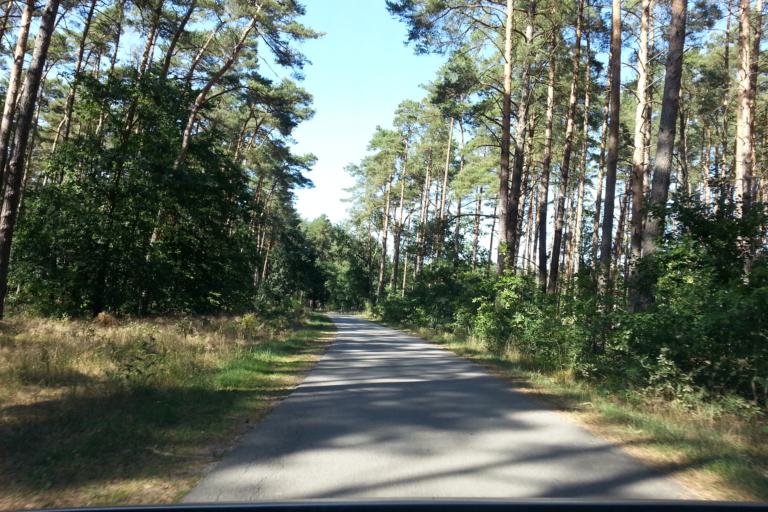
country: DE
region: Mecklenburg-Vorpommern
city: Torgelow
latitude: 53.6603
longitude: 14.0339
